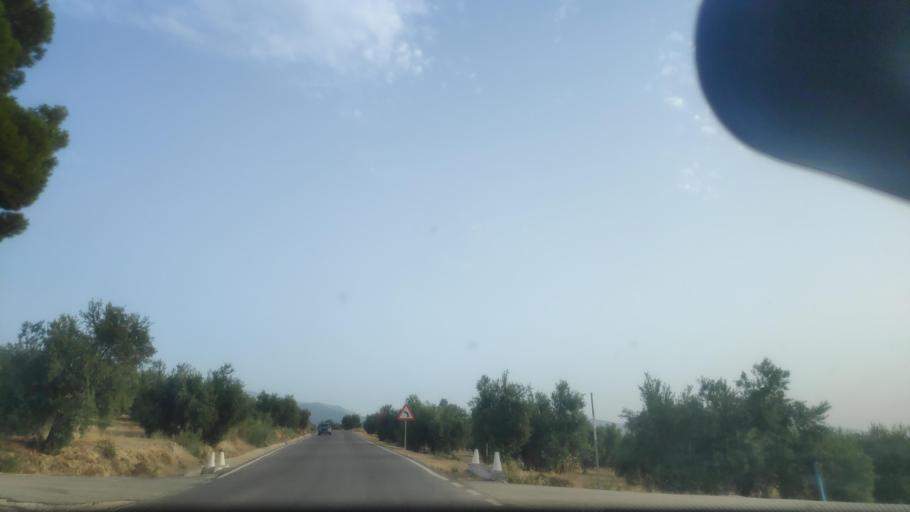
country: ES
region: Andalusia
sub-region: Provincia de Jaen
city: Jimena
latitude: 37.8377
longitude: -3.5300
